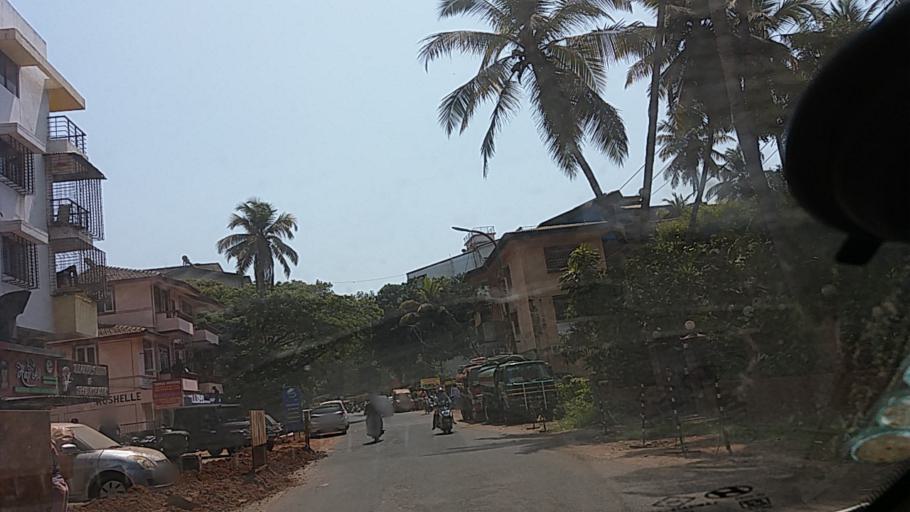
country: IN
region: Goa
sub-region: North Goa
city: Panaji
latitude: 15.4867
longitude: 73.8196
